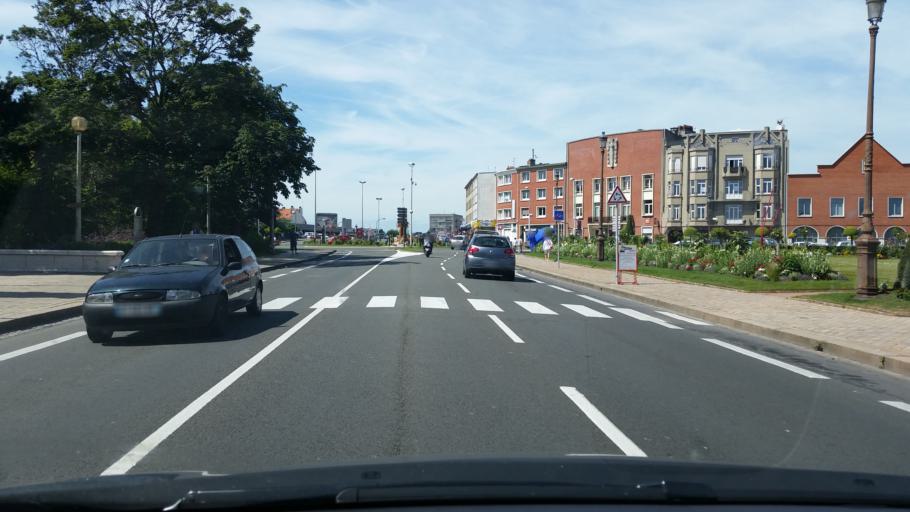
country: FR
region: Nord-Pas-de-Calais
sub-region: Departement du Pas-de-Calais
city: Calais
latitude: 50.9522
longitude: 1.8530
